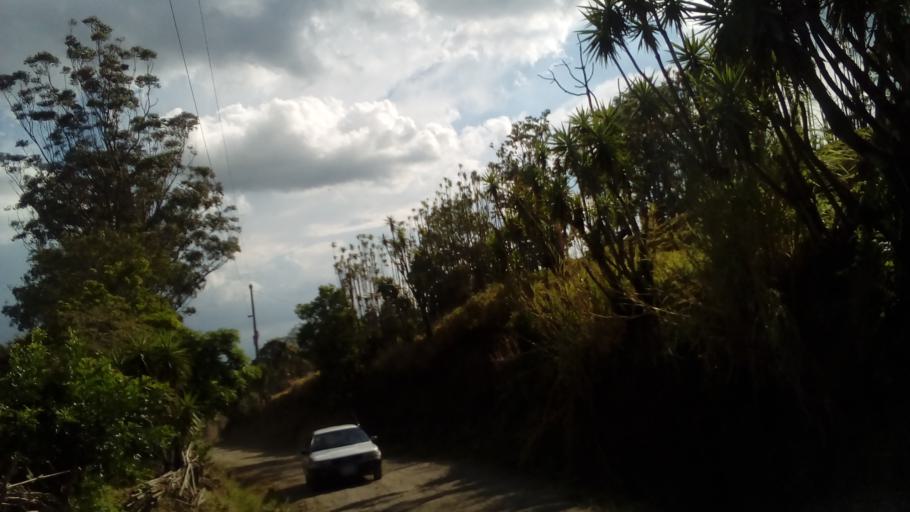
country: CR
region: Alajuela
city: San Juan
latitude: 10.1244
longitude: -84.2619
